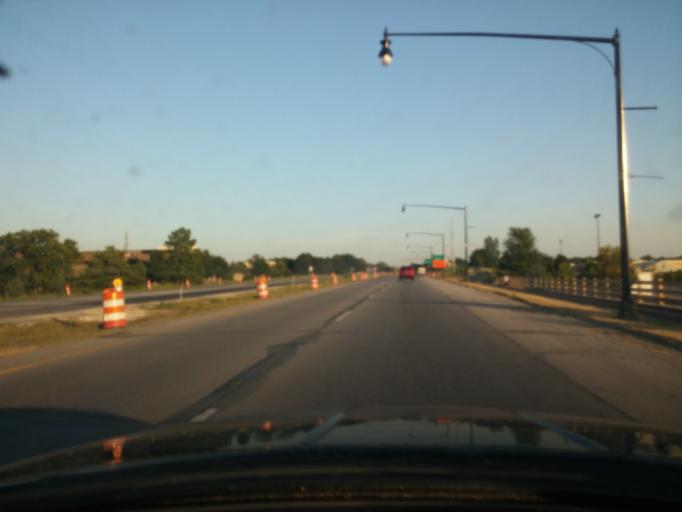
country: US
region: Indiana
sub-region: Tippecanoe County
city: West Lafayette
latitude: 40.4597
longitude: -86.9328
